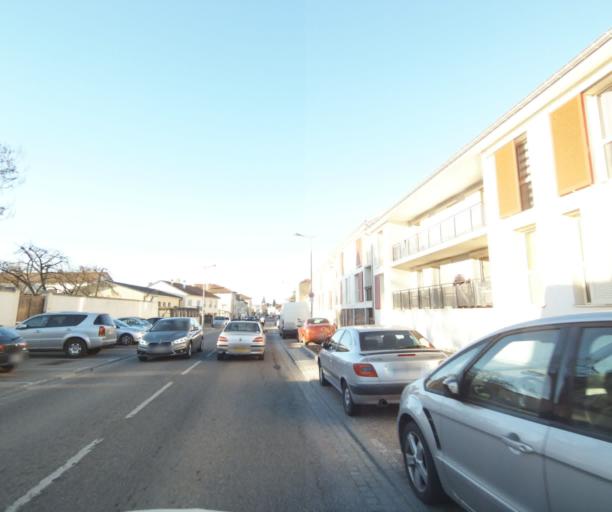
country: FR
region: Lorraine
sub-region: Departement de Meurthe-et-Moselle
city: Laneuveville-devant-Nancy
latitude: 48.6535
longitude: 6.2329
